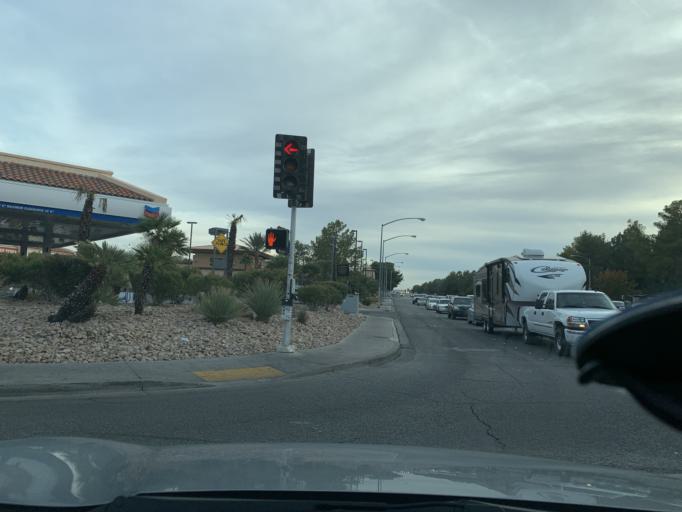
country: US
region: Nevada
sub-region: Clark County
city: Spring Valley
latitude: 36.0997
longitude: -115.2430
